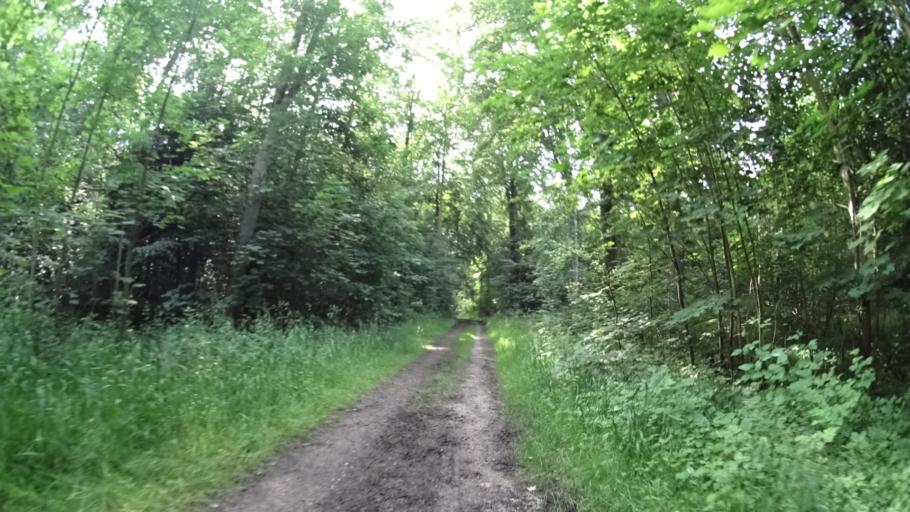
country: DK
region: Central Jutland
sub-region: Arhus Kommune
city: Stavtrup
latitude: 56.1385
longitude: 10.0934
